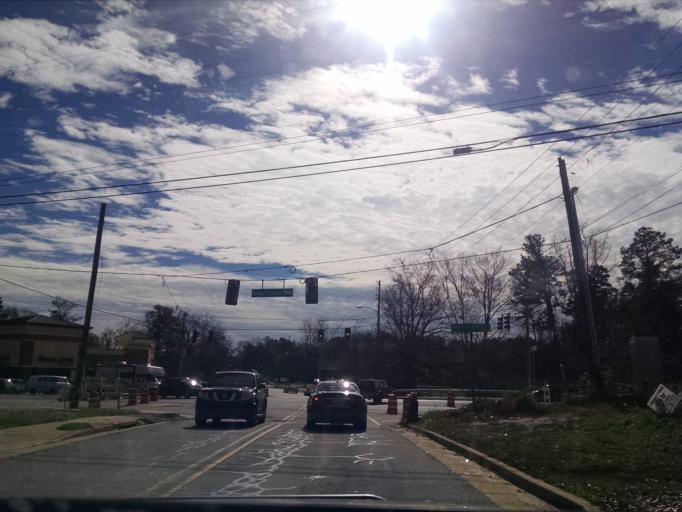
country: US
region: Georgia
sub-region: Gwinnett County
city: Sugar Hill
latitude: 34.1118
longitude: -84.0404
